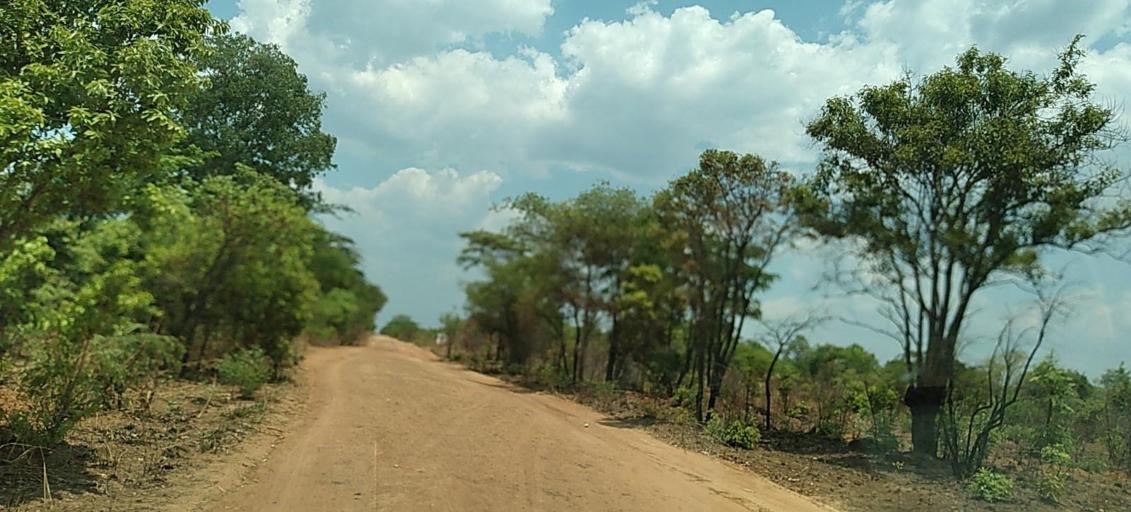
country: ZM
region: Copperbelt
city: Luanshya
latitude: -13.3799
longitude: 28.4339
